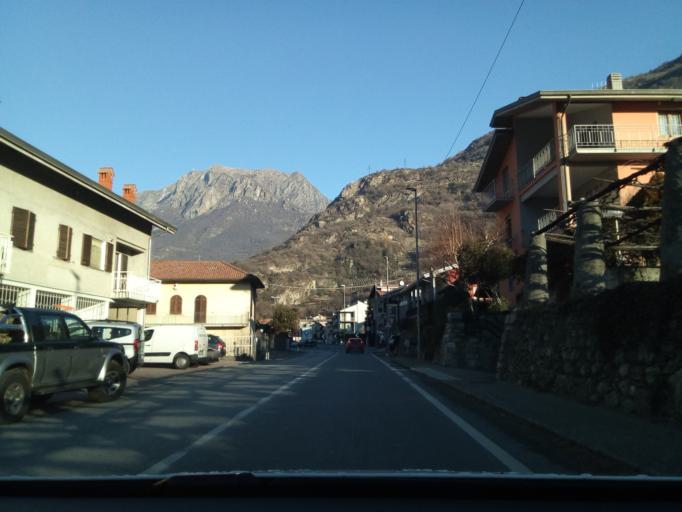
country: IT
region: Piedmont
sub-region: Provincia di Torino
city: Carema
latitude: 45.5815
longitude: 7.8084
